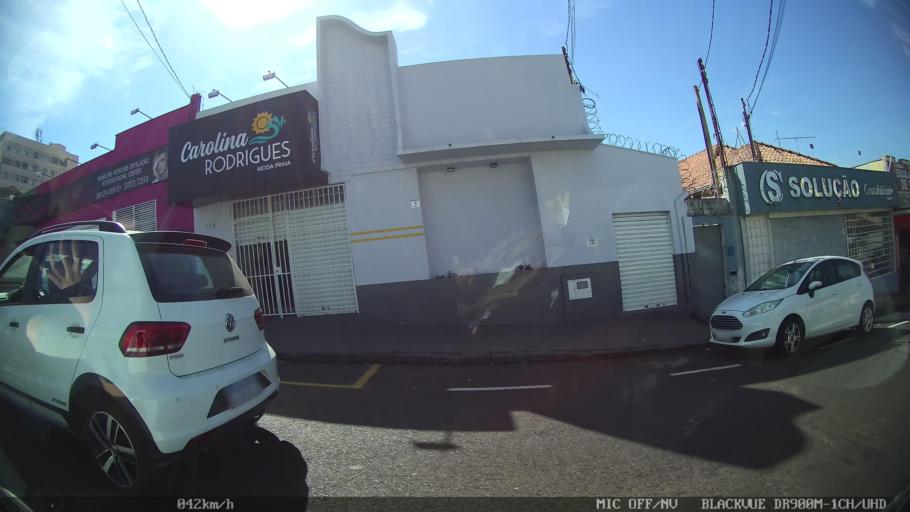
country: BR
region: Sao Paulo
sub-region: Franca
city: Franca
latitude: -20.5349
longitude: -47.4077
